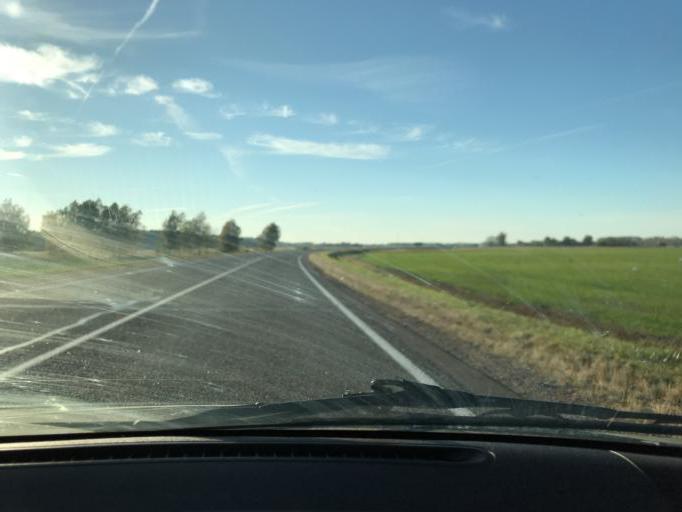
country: BY
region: Brest
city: Horad Kobryn
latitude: 52.2098
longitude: 24.4743
